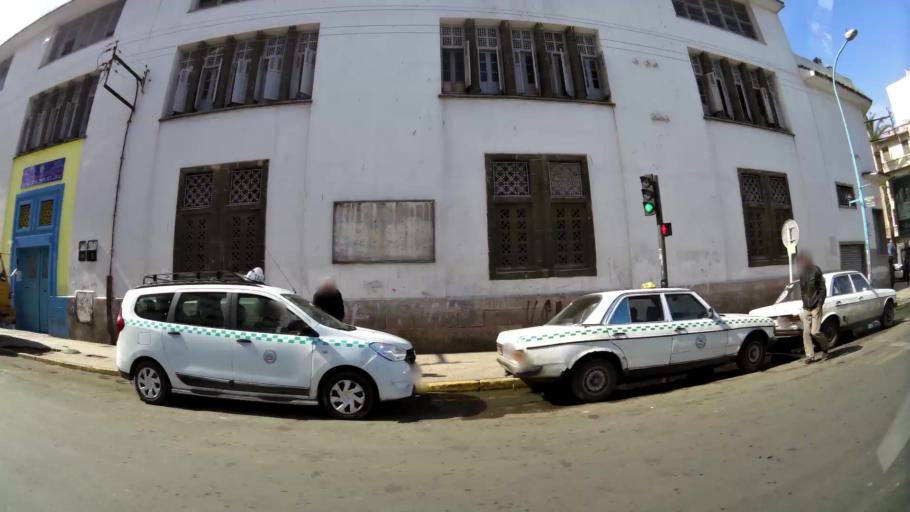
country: MA
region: Grand Casablanca
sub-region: Casablanca
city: Casablanca
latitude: 33.5948
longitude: -7.6232
